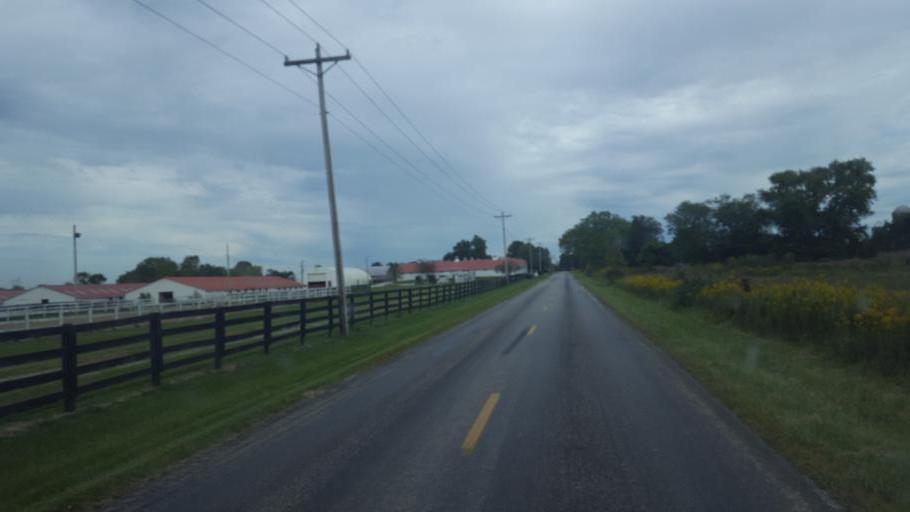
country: US
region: Ohio
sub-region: Knox County
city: Centerburg
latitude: 40.2613
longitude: -82.7580
